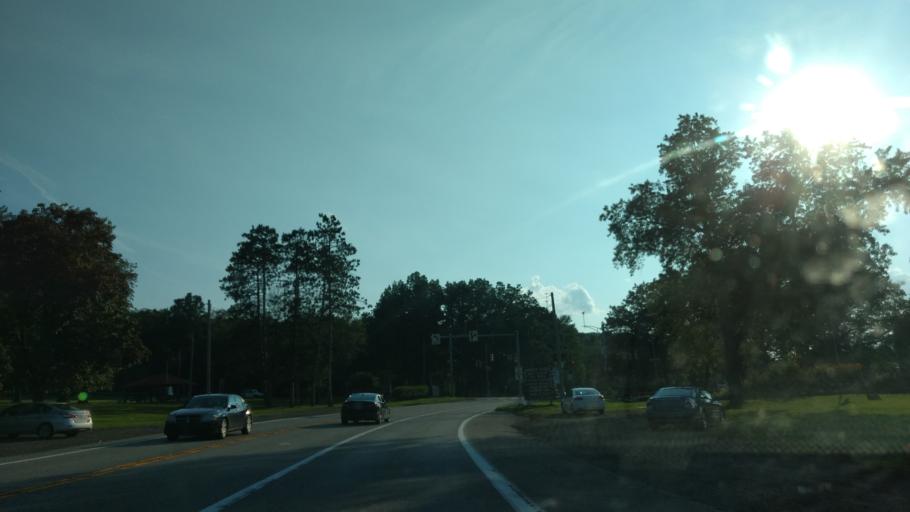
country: US
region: Pennsylvania
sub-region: Allegheny County
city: Gibsonia
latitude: 40.5943
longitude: -79.9954
